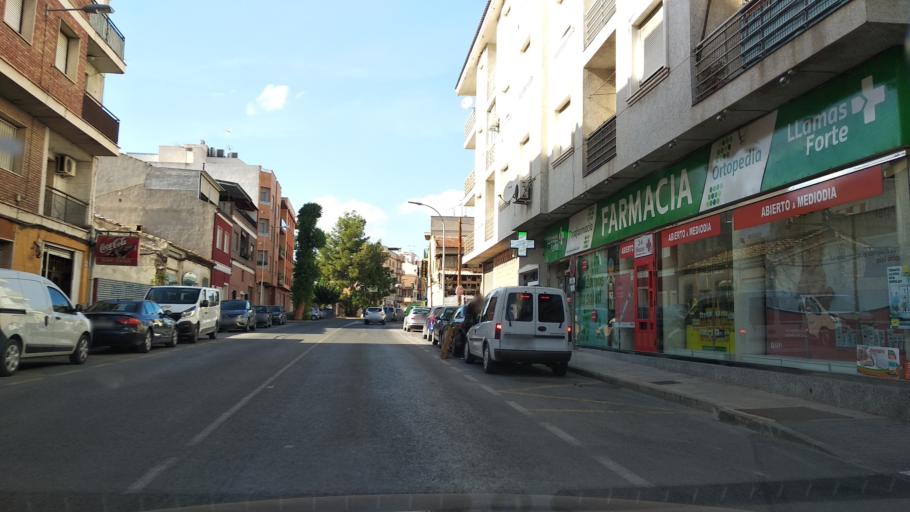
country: ES
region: Murcia
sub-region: Murcia
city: Santomera
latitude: 38.0612
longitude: -1.0530
